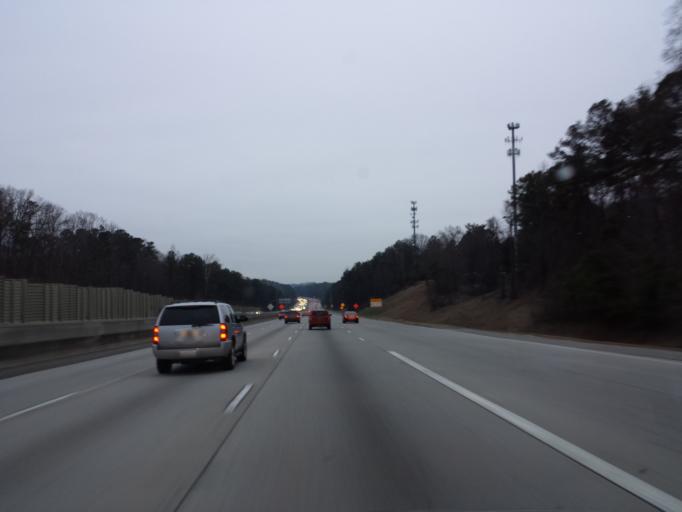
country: US
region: Georgia
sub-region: Fulton County
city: Roswell
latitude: 34.0174
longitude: -84.3276
